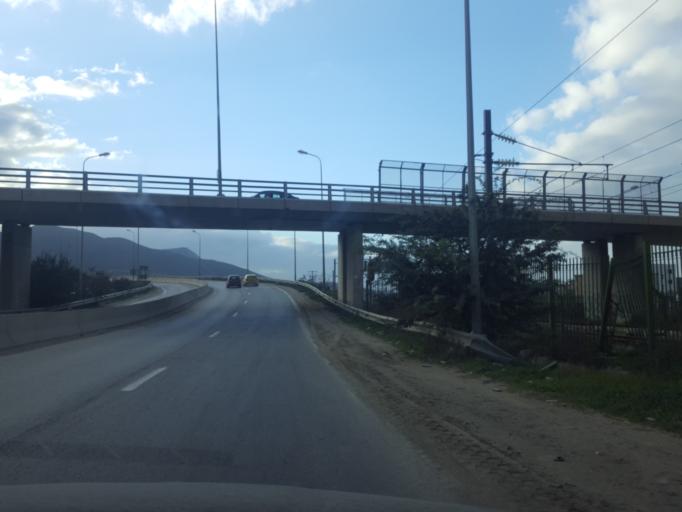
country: TN
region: Tunis
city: Hammam-Lif
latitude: 36.7011
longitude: 10.4051
